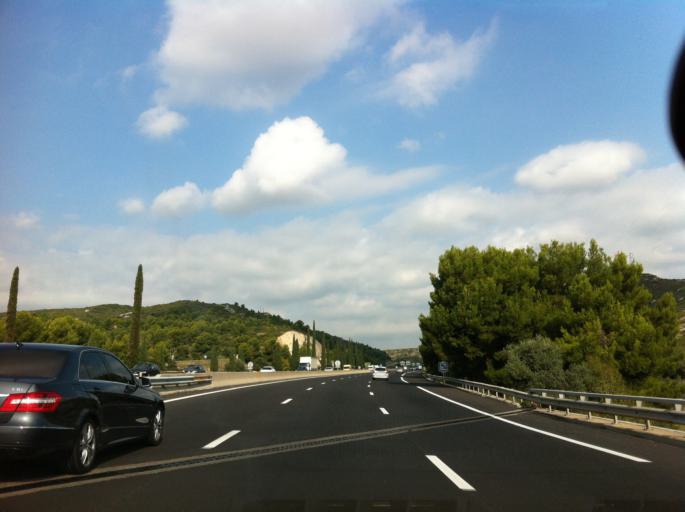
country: FR
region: Provence-Alpes-Cote d'Azur
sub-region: Departement des Bouches-du-Rhone
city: Coudoux
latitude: 43.5552
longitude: 5.2314
